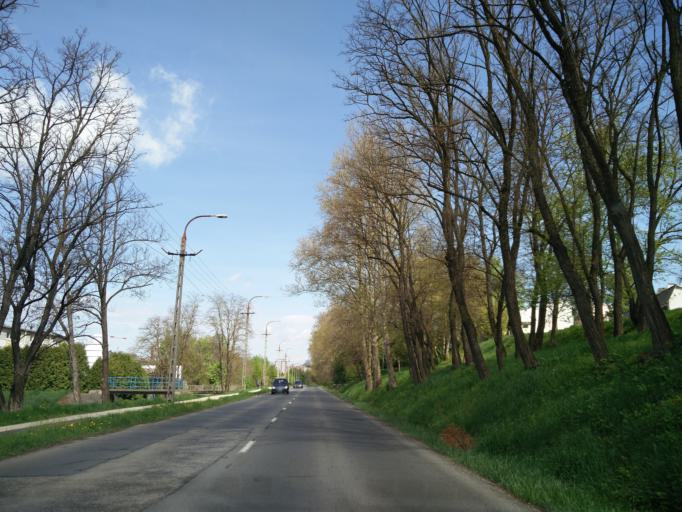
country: HU
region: Zala
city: Zalaegerszeg
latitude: 46.8249
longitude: 16.8283
